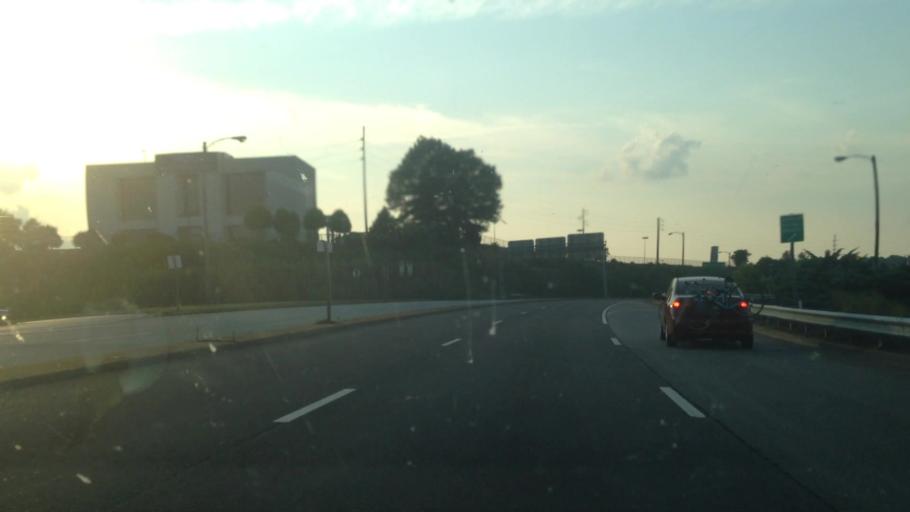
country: US
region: Virginia
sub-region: City of Danville
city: Danville
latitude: 36.5922
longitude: -79.4169
